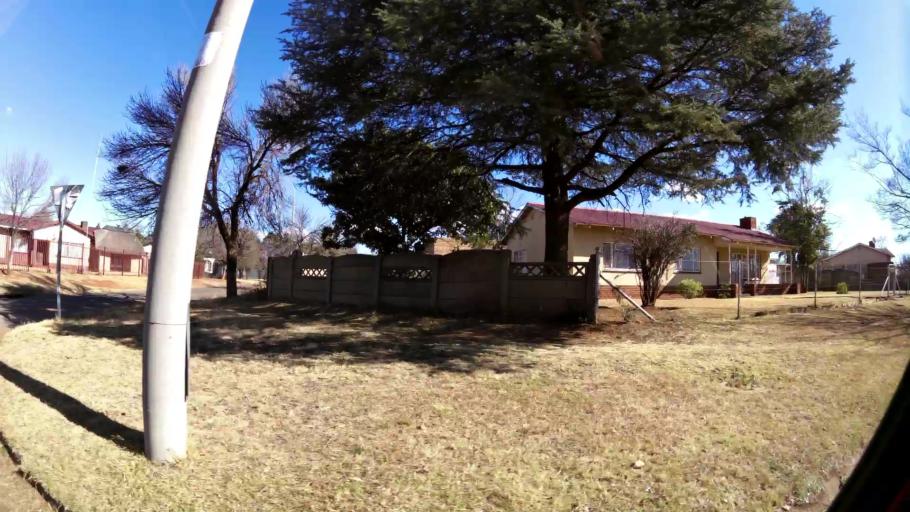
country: ZA
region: Gauteng
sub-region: West Rand District Municipality
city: Carletonville
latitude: -26.3630
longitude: 27.3824
